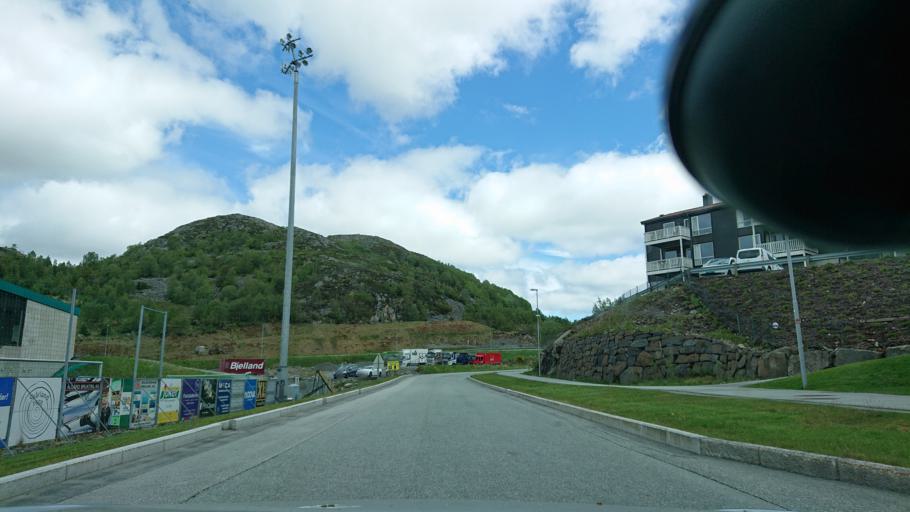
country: NO
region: Rogaland
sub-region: Gjesdal
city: Algard
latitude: 58.7747
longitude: 5.8684
